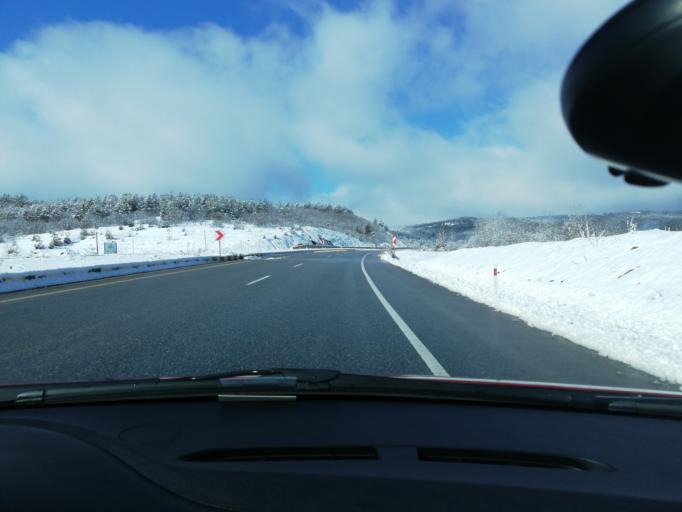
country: TR
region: Kastamonu
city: Kuzyaka
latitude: 41.3357
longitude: 33.6384
